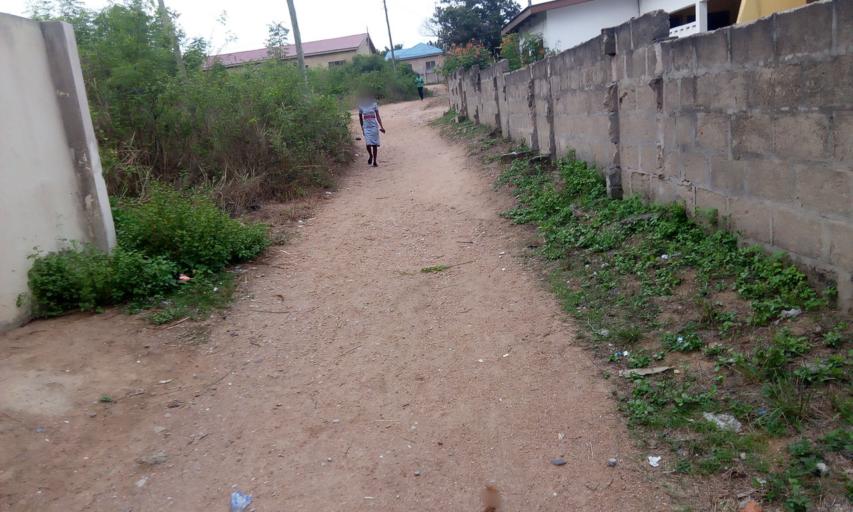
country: GH
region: Central
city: Winneba
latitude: 5.3543
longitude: -0.6243
